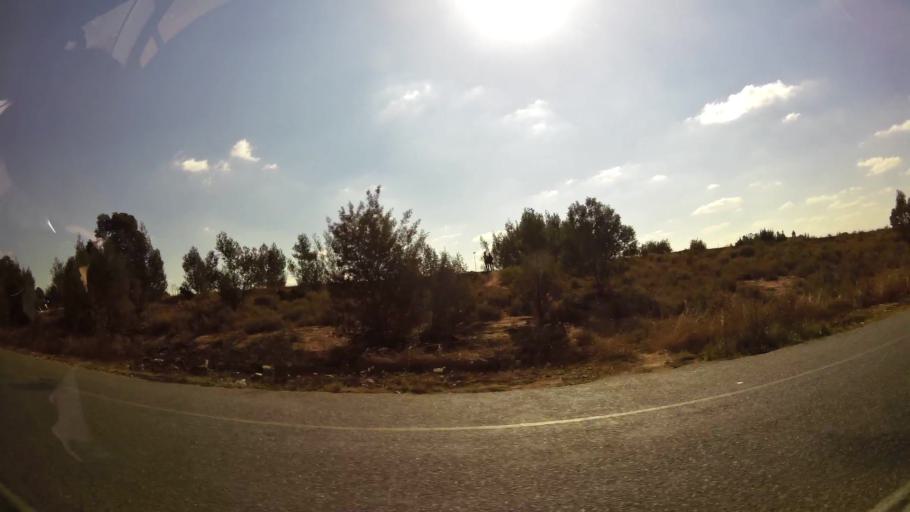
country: ZA
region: Gauteng
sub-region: West Rand District Municipality
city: Randfontein
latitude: -26.1808
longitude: 27.7558
